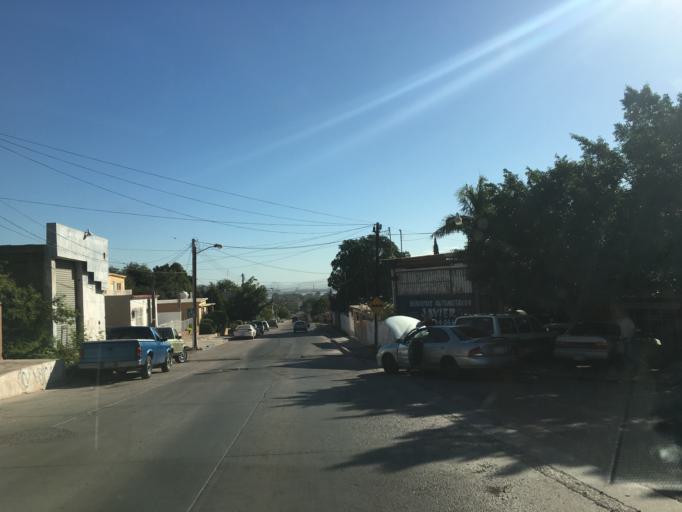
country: MX
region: Sonora
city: Heroica Guaymas
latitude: 27.9168
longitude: -110.9068
